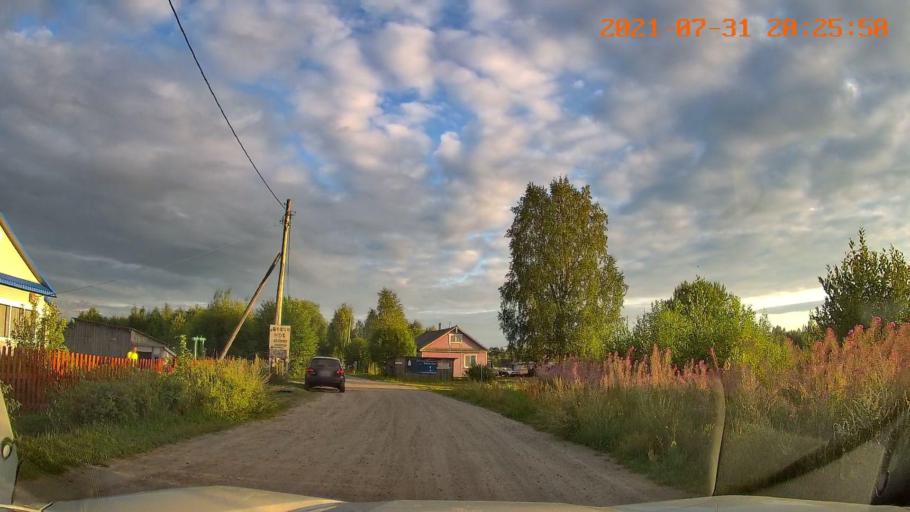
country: RU
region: Republic of Karelia
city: Pudozh
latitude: 61.6743
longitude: 36.3079
